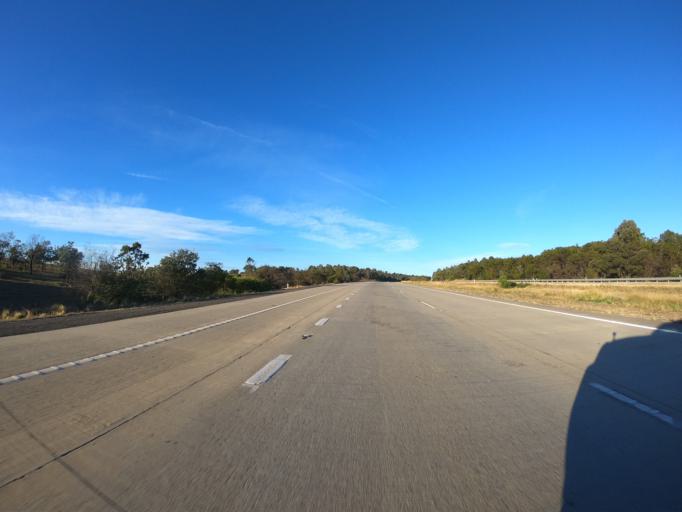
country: AU
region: New South Wales
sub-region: Yass Valley
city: Gundaroo
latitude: -35.1043
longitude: 149.3729
